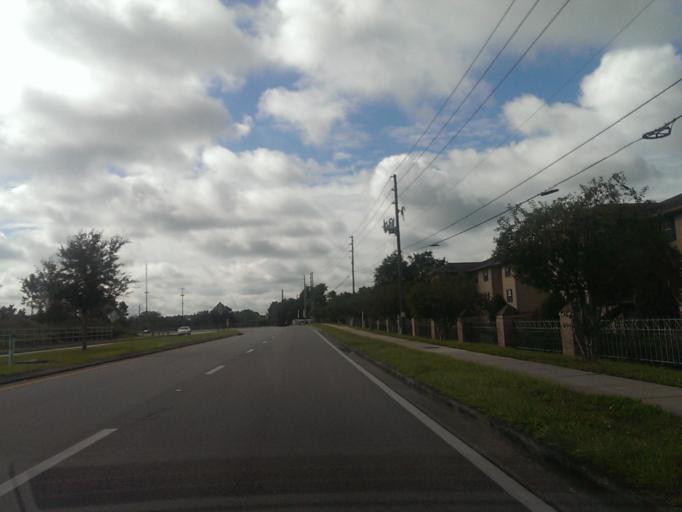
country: US
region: Florida
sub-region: Orange County
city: Doctor Phillips
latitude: 28.4022
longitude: -81.5329
